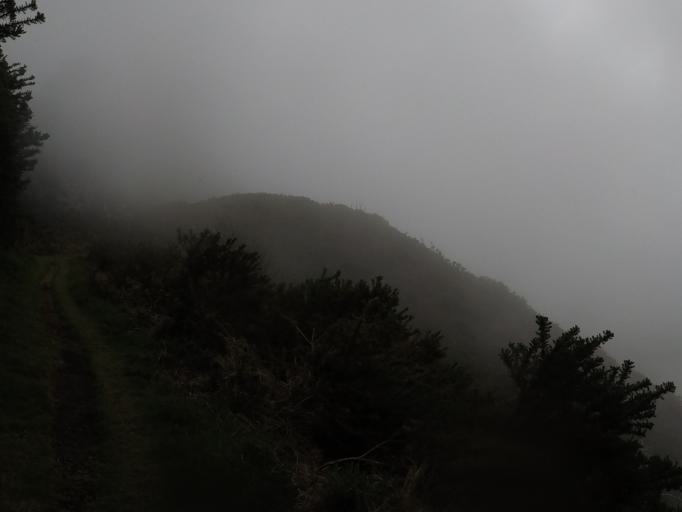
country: PT
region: Madeira
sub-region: Camara de Lobos
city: Curral das Freiras
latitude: 32.7298
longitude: -16.9855
